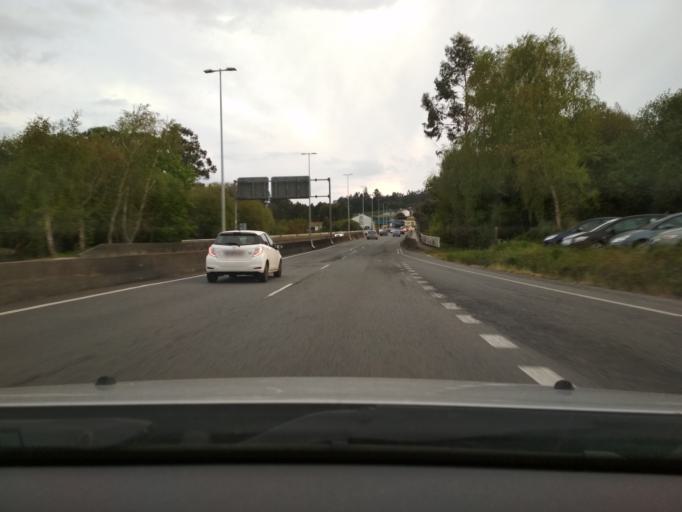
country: ES
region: Galicia
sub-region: Provincia da Coruna
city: Santiago de Compostela
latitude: 42.8624
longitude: -8.5691
